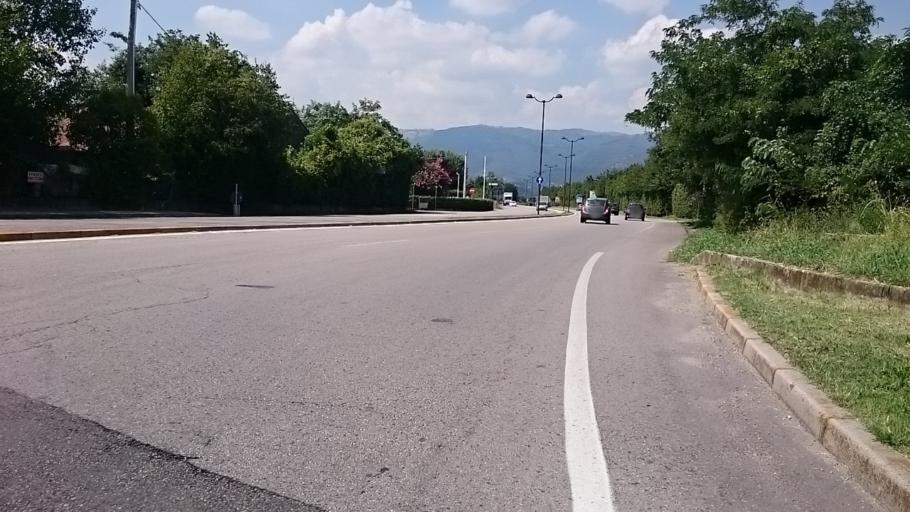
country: IT
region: Veneto
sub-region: Provincia di Vicenza
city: Bassano del Grappa
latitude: 45.7435
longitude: 11.7303
